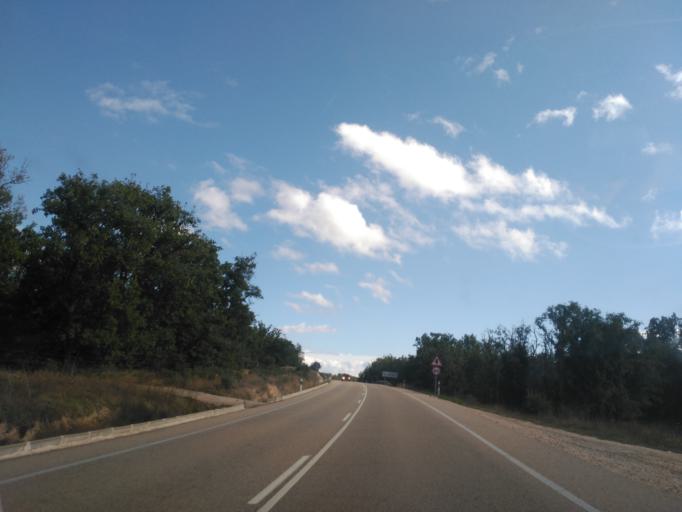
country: ES
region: Castille and Leon
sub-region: Provincia de Burgos
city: Pinilla de los Barruecos
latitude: 41.9290
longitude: -3.2819
